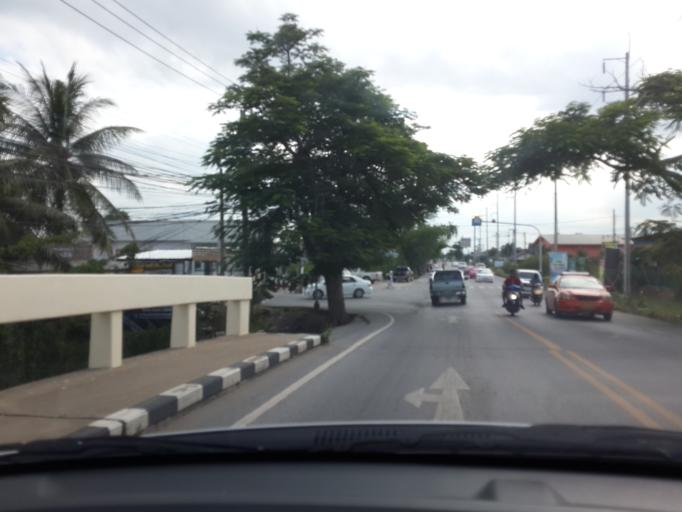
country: TH
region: Bangkok
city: Khlong Sam Wa
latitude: 13.8422
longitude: 100.7808
